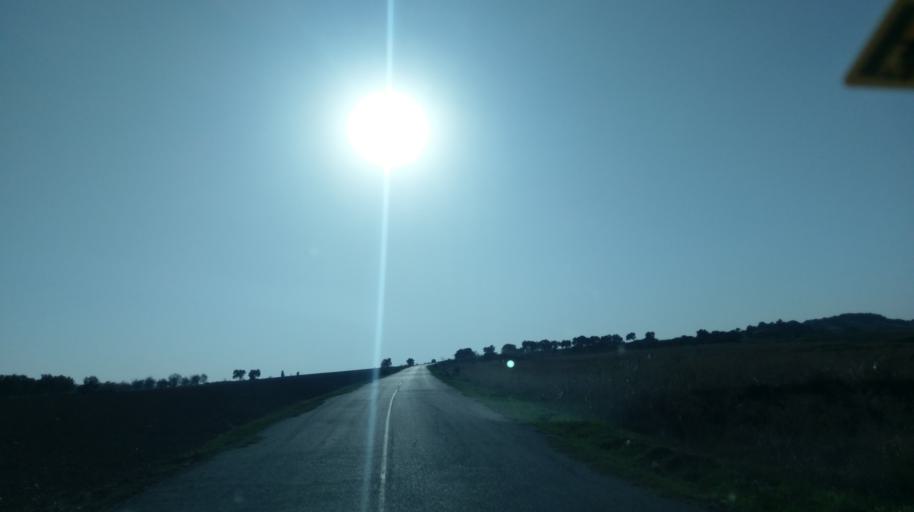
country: CY
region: Ammochostos
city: Leonarisso
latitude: 35.4388
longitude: 34.0870
